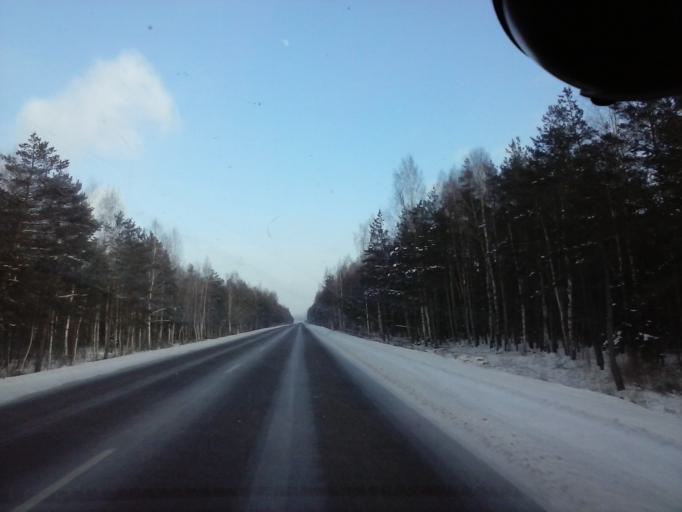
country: EE
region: Tartu
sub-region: Puhja vald
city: Puhja
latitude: 58.3271
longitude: 26.2389
